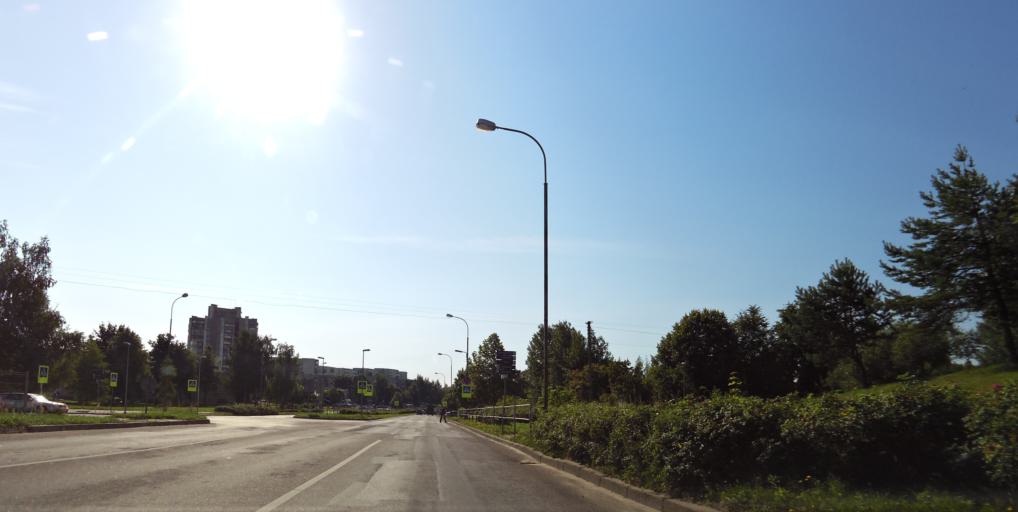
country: LT
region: Vilnius County
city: Seskine
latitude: 54.7148
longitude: 25.2349
